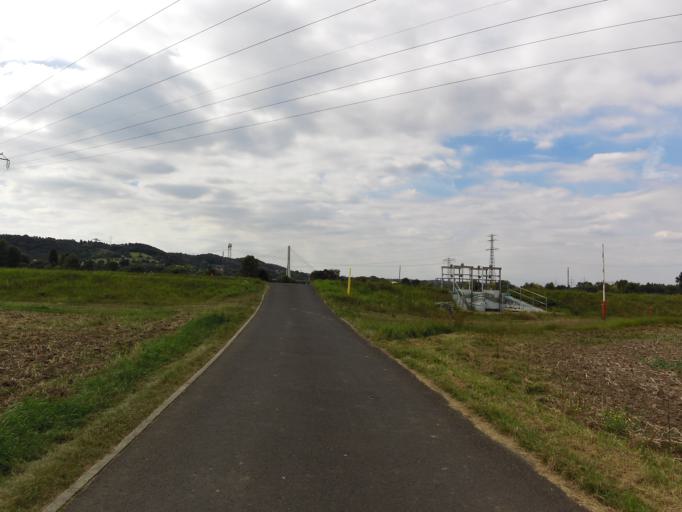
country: DE
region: Saxony
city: Radebeul
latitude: 51.0969
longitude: 13.6173
